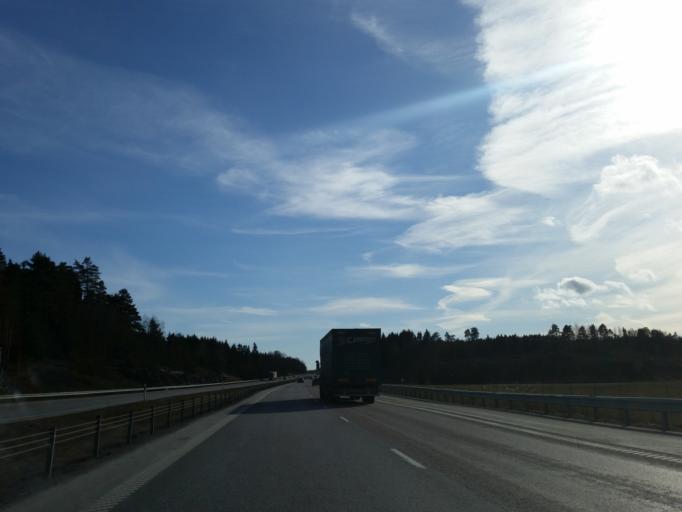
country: SE
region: Soedermanland
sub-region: Trosa Kommun
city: Vagnharad
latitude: 59.0382
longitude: 17.5627
